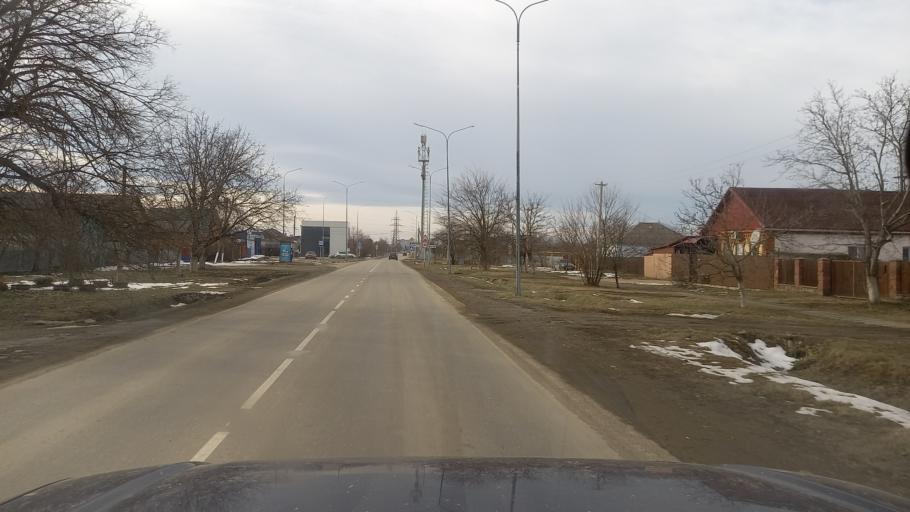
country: RU
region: Krasnodarskiy
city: Belorechensk
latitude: 44.7616
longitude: 39.8939
